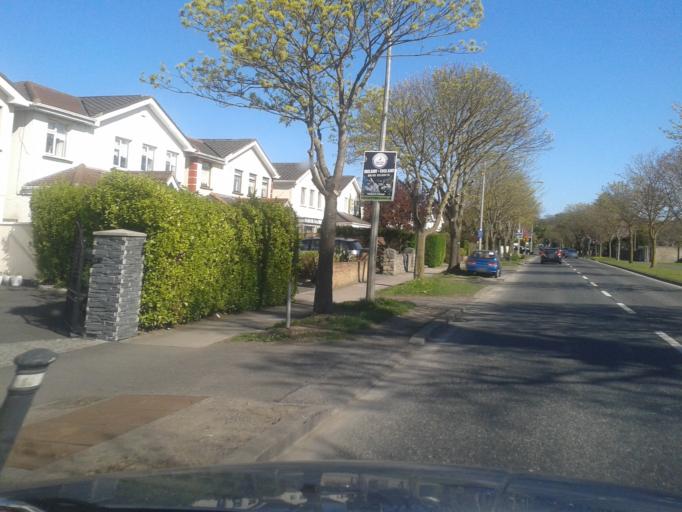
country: IE
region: Leinster
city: Kinsealy-Drinan
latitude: 53.4481
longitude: -6.1794
